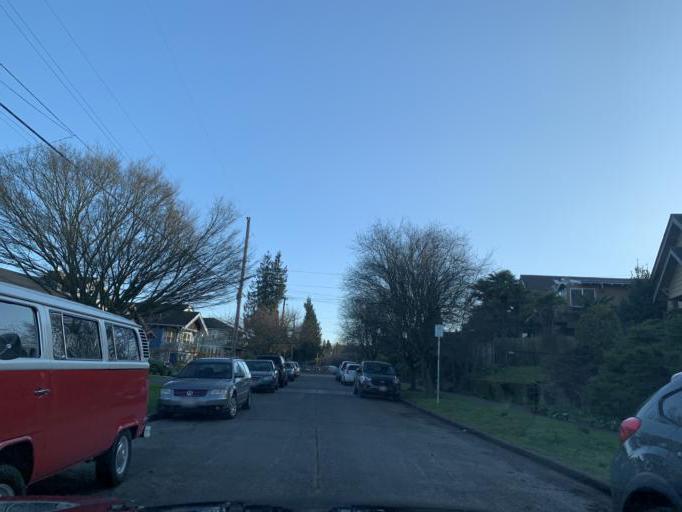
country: US
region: Washington
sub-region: King County
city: Seattle
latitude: 47.5759
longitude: -122.3077
